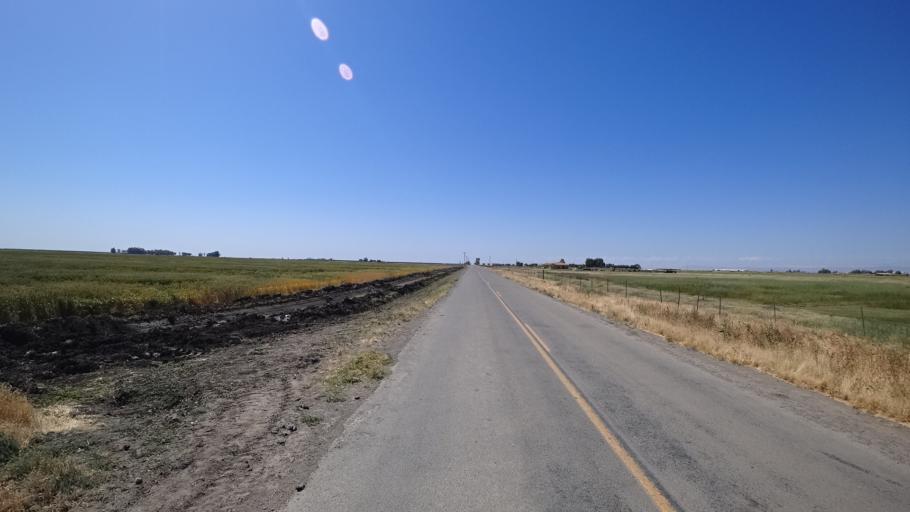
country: US
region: California
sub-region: Kings County
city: Stratford
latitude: 36.1819
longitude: -119.7803
